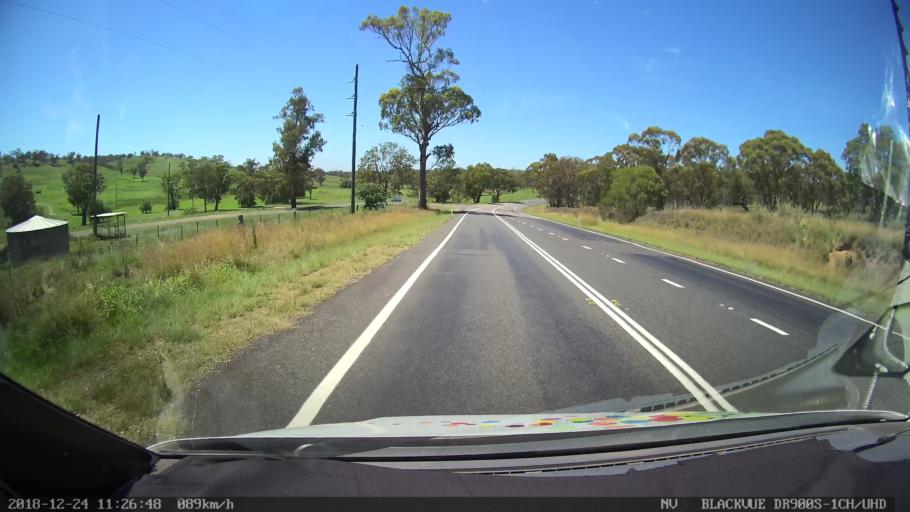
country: AU
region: New South Wales
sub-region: Upper Hunter Shire
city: Merriwa
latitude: -32.1736
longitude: 150.4333
